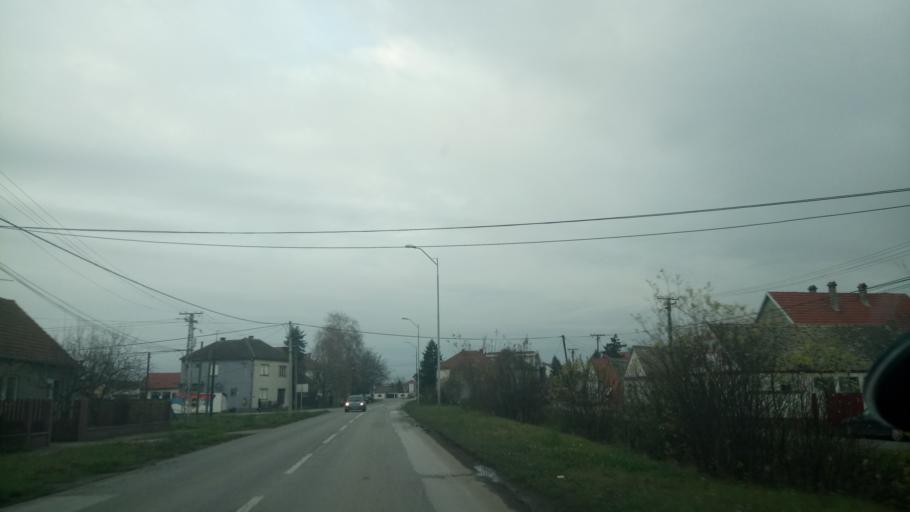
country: RS
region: Autonomna Pokrajina Vojvodina
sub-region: Sremski Okrug
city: Stara Pazova
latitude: 44.9757
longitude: 20.1647
